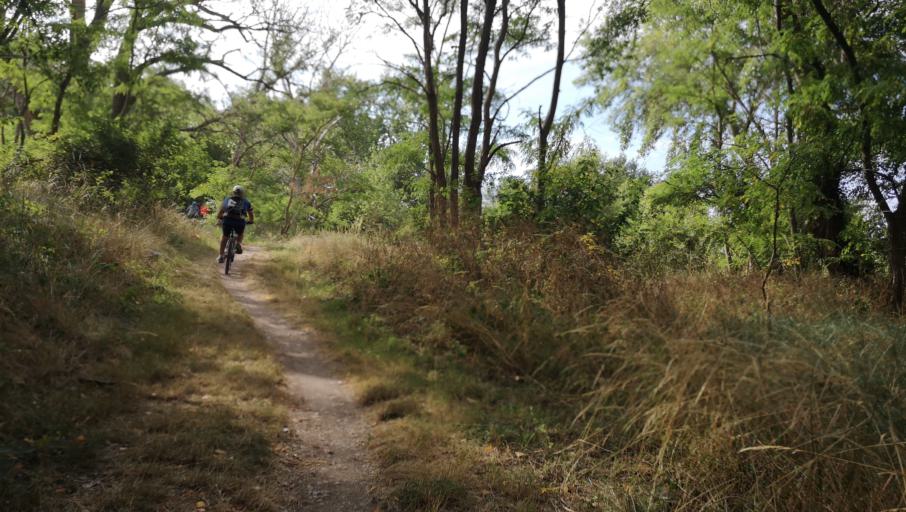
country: FR
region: Centre
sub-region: Departement du Loiret
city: Sandillon
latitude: 47.8576
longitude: 2.0359
